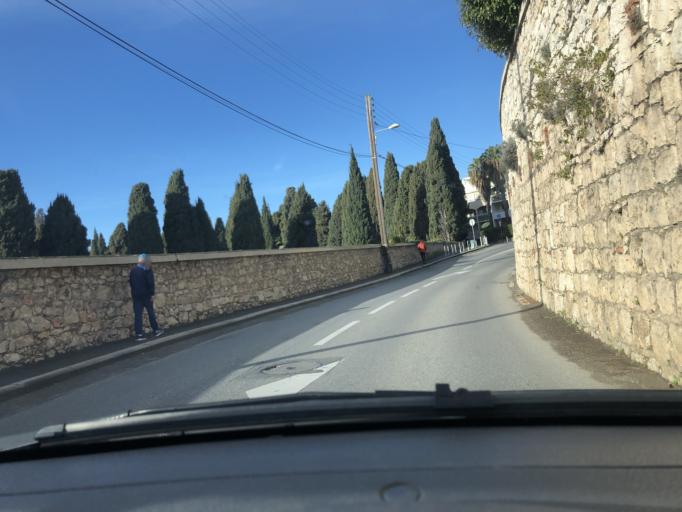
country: FR
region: Provence-Alpes-Cote d'Azur
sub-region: Departement des Alpes-Maritimes
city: Saint-Laurent-du-Var
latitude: 43.6774
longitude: 7.2162
